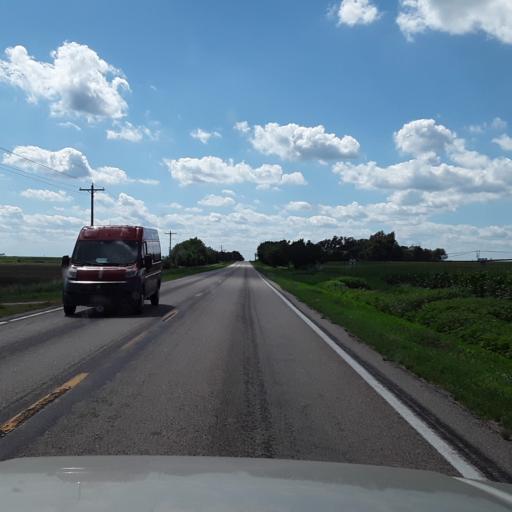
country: US
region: Nebraska
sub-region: Merrick County
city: Central City
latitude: 41.1910
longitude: -98.0112
